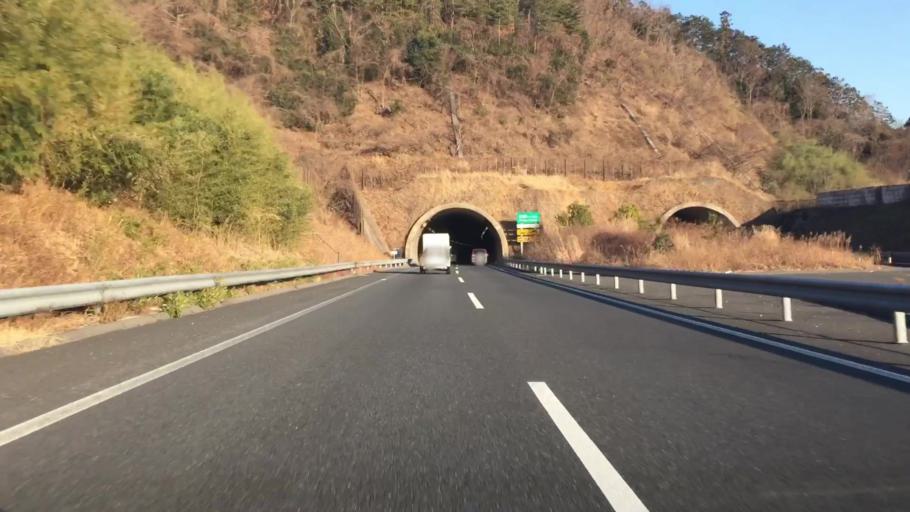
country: JP
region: Tochigi
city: Ashikaga
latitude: 36.3681
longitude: 139.4596
